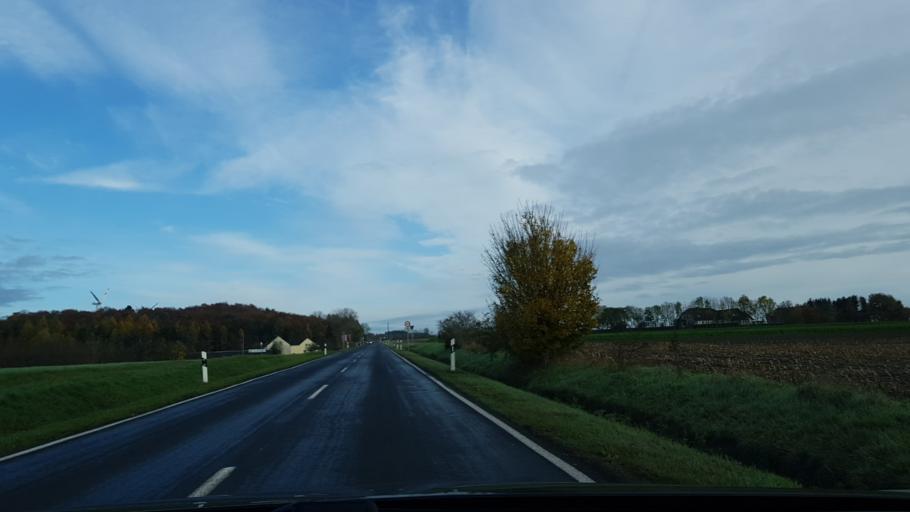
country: DE
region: Rheinland-Pfalz
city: Bitburg
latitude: 49.9846
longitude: 6.5280
